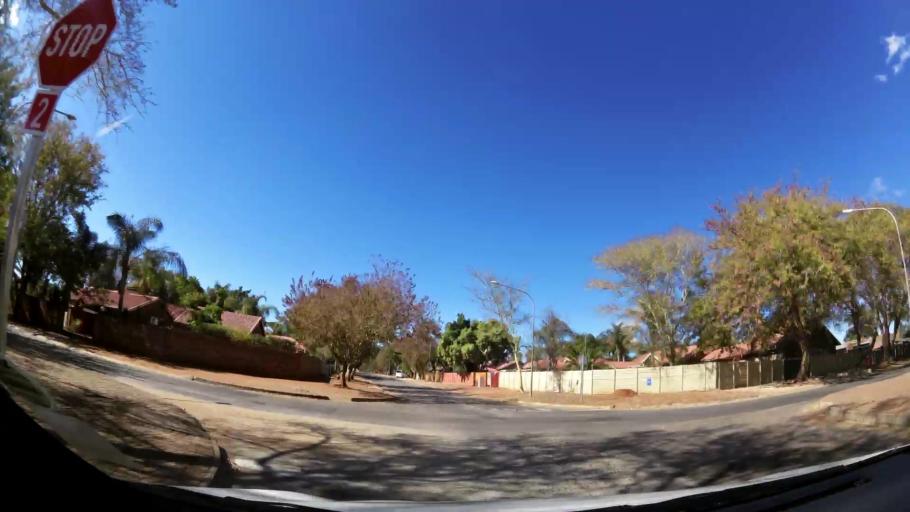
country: ZA
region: Limpopo
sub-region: Capricorn District Municipality
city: Polokwane
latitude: -23.9168
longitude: 29.4878
